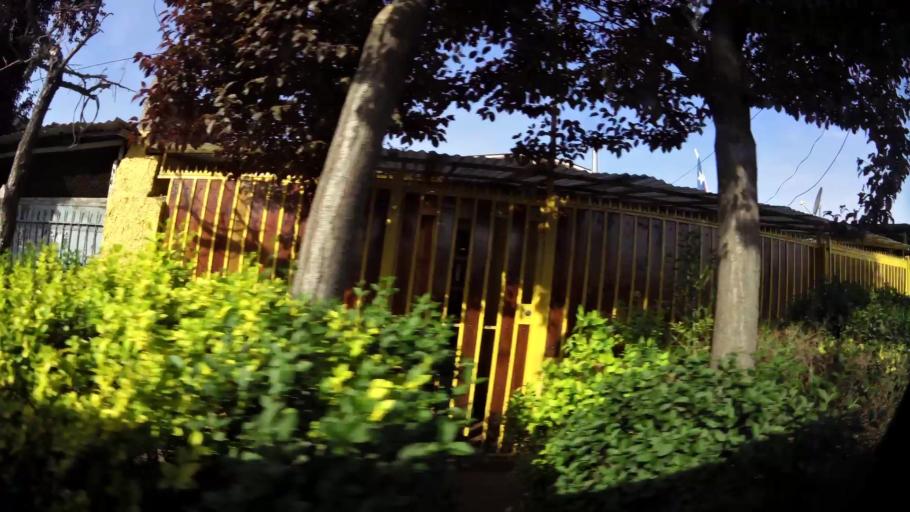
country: CL
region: Santiago Metropolitan
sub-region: Provincia de Santiago
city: Santiago
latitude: -33.5123
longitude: -70.6257
